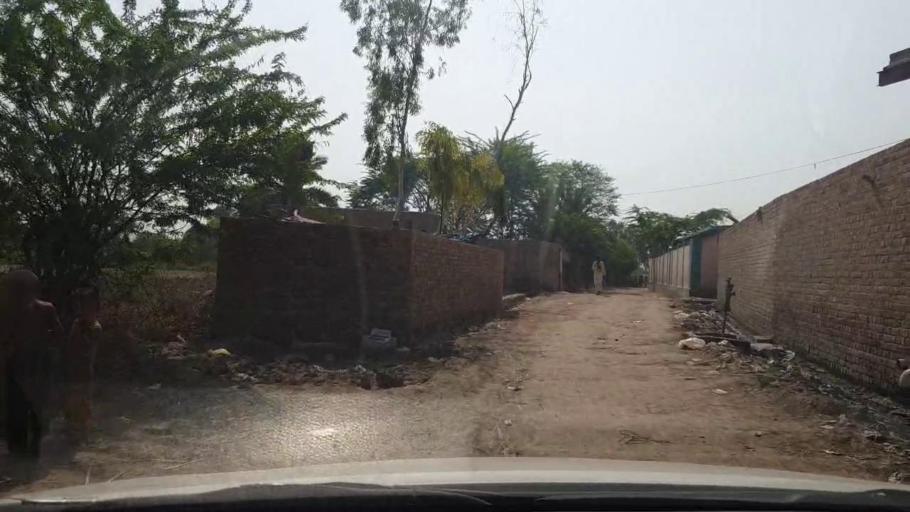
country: PK
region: Sindh
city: Shikarpur
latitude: 27.9755
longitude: 68.6761
